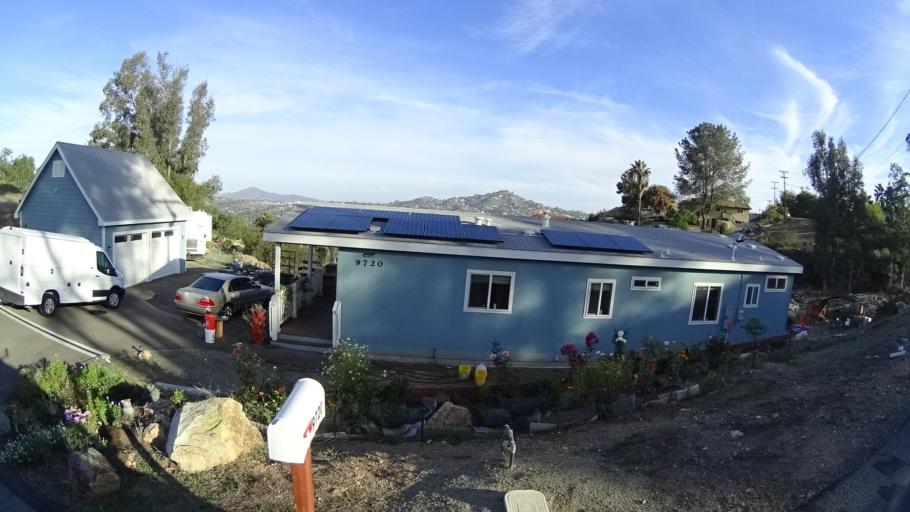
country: US
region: California
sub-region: San Diego County
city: Spring Valley
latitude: 32.7351
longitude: -116.9880
